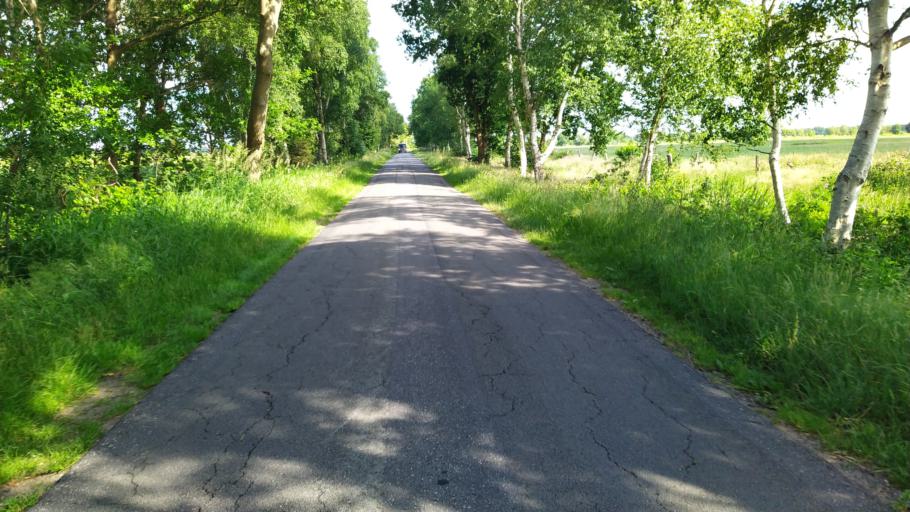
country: DE
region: Lower Saxony
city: Steinau
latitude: 53.6495
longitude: 8.9042
